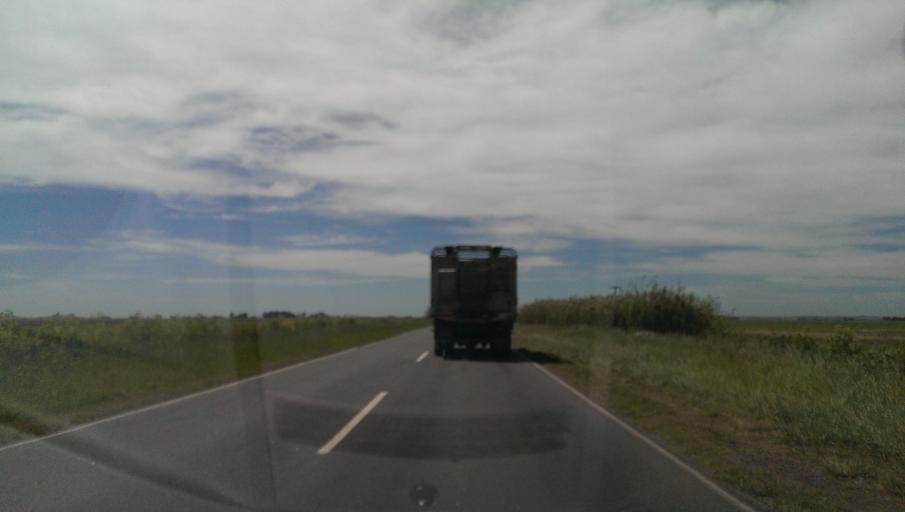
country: AR
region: Buenos Aires
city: Olavarria
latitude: -37.0599
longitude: -60.4583
